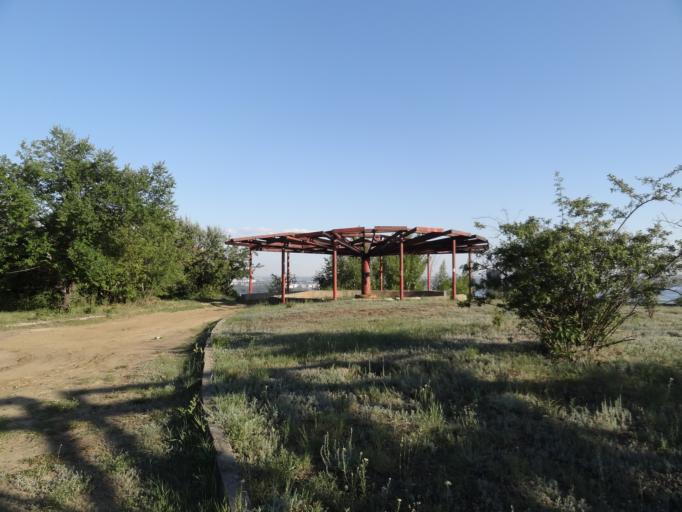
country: RU
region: Saratov
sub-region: Saratovskiy Rayon
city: Saratov
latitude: 51.5396
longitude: 46.0638
